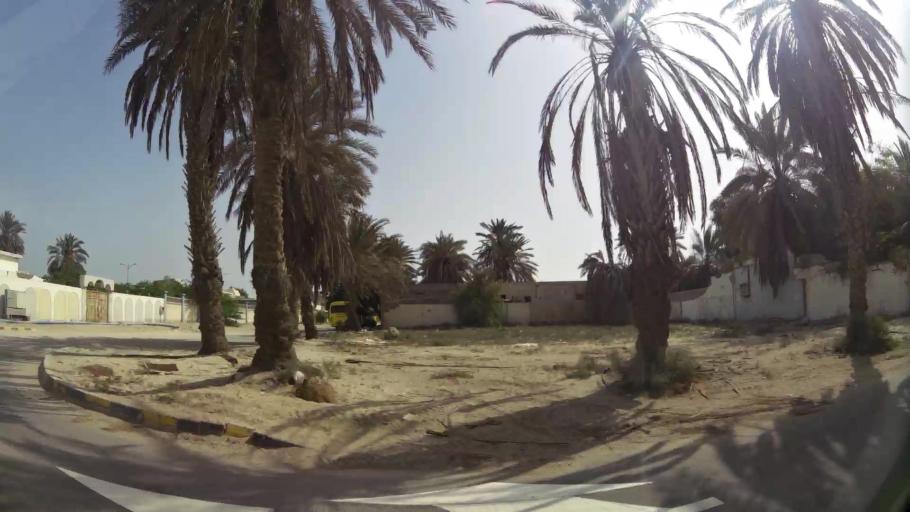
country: AE
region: Ash Shariqah
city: Sharjah
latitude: 25.3492
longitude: 55.4100
